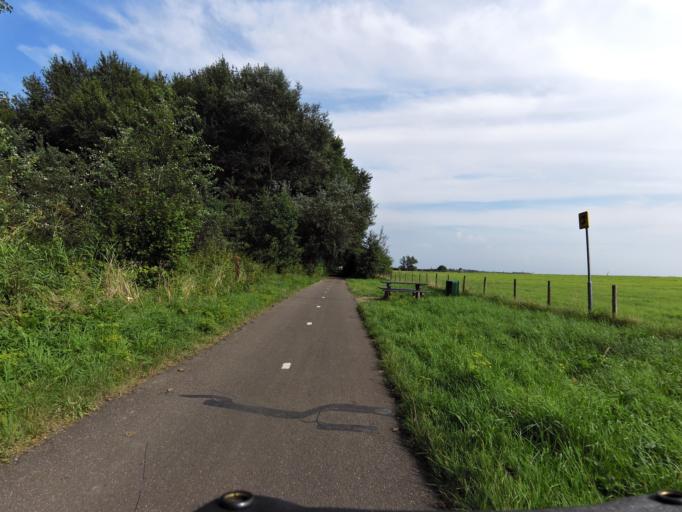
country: NL
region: South Holland
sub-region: Gemeente Barendrecht
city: Barendrecht
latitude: 51.8255
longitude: 4.5214
